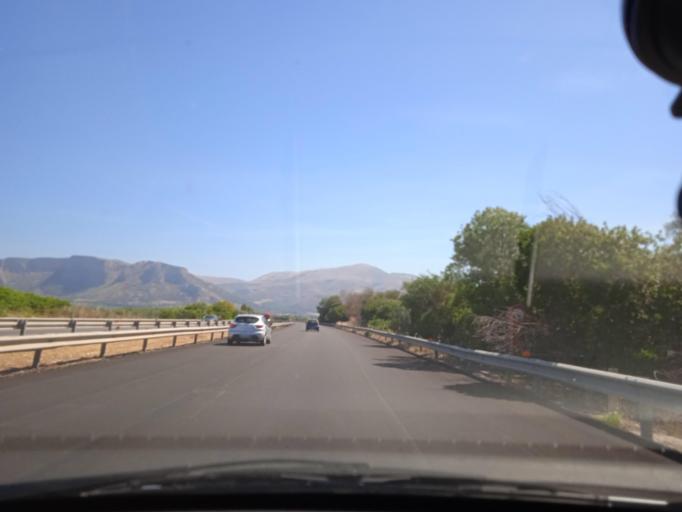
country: IT
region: Sicily
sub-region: Palermo
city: Trappeto
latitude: 38.0567
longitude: 13.0747
